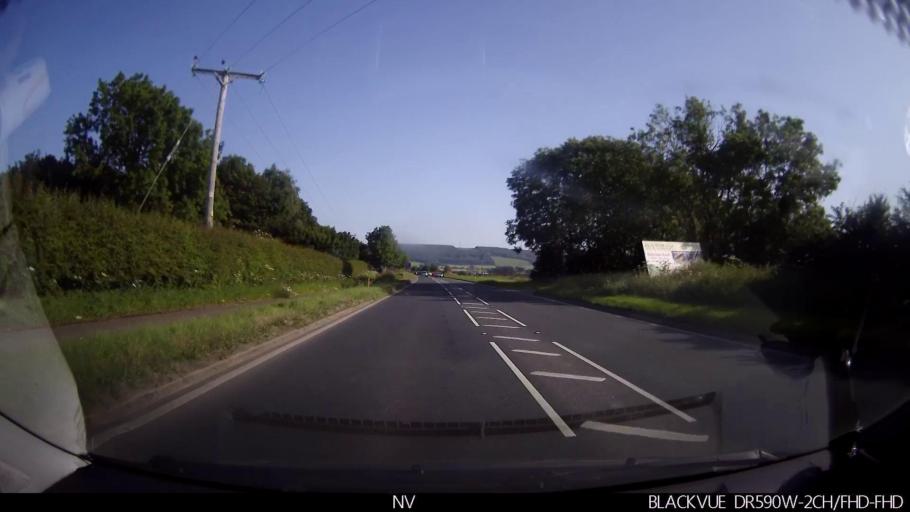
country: GB
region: England
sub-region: North Yorkshire
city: East Ayton
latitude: 54.2169
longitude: -0.4384
